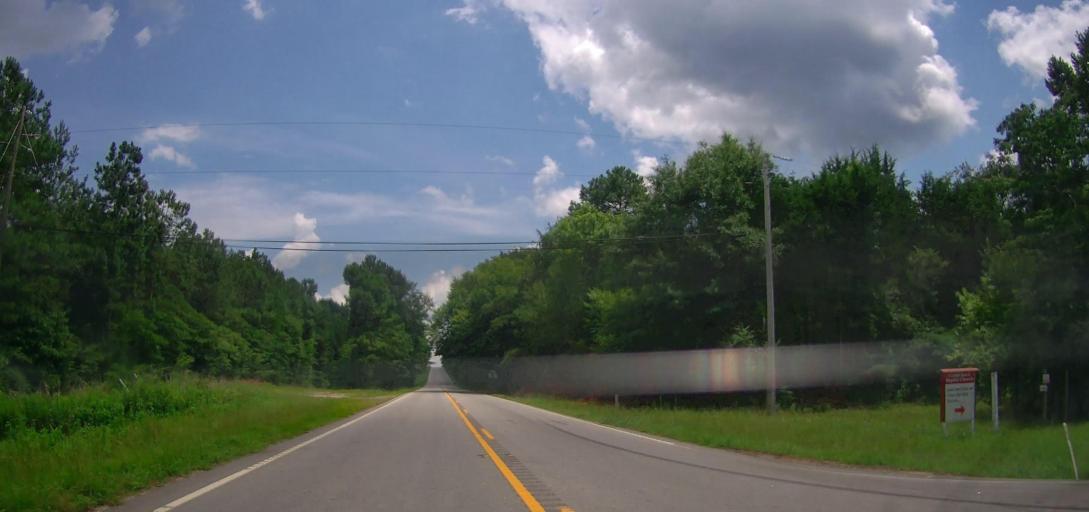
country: US
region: Georgia
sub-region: Meriwether County
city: Greenville
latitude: 32.9930
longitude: -84.6269
